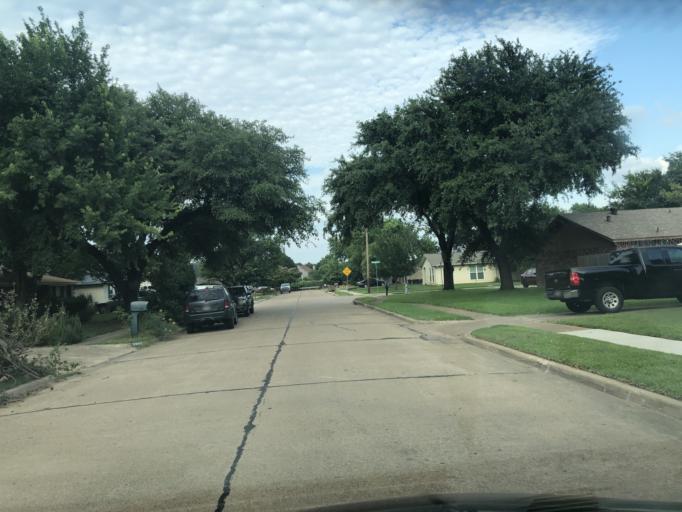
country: US
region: Texas
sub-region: Dallas County
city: Irving
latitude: 32.7899
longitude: -96.9701
